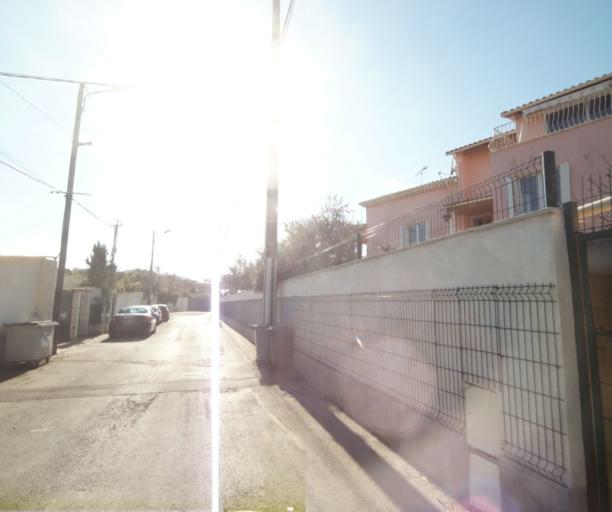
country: FR
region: Provence-Alpes-Cote d'Azur
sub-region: Departement des Alpes-Maritimes
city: Biot
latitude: 43.6140
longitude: 7.1180
